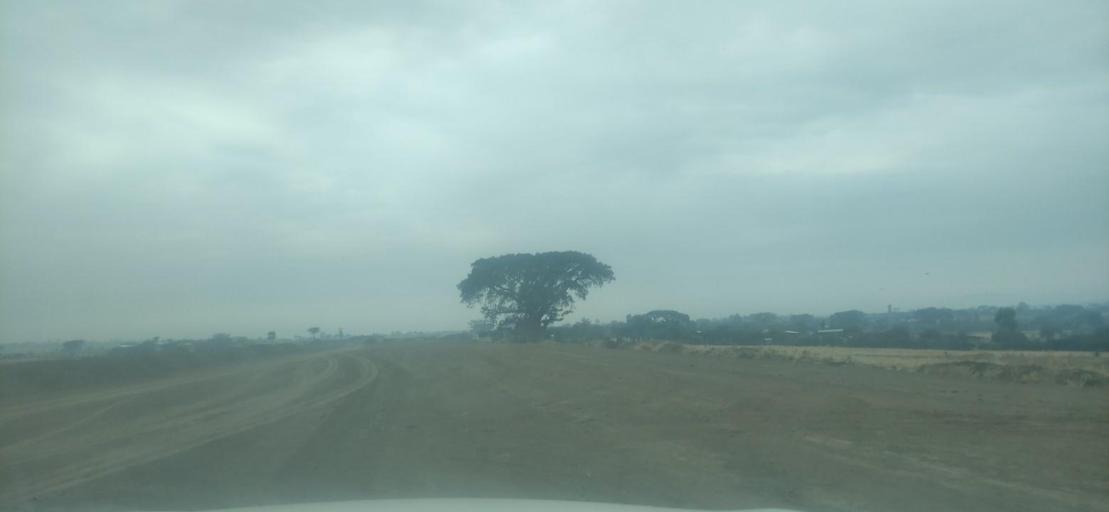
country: ET
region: Oromiya
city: Shashemene
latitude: 7.3782
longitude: 38.6470
